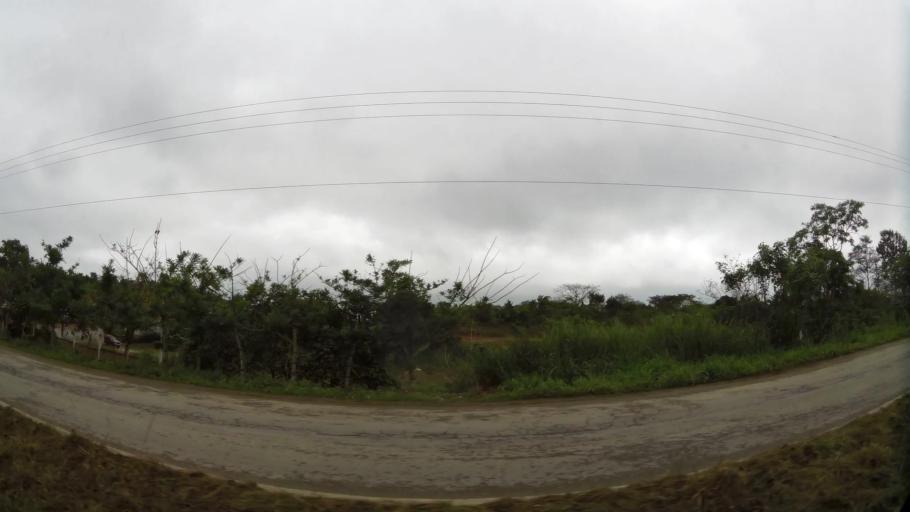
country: EC
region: El Oro
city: Pasaje
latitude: -3.3357
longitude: -79.7904
